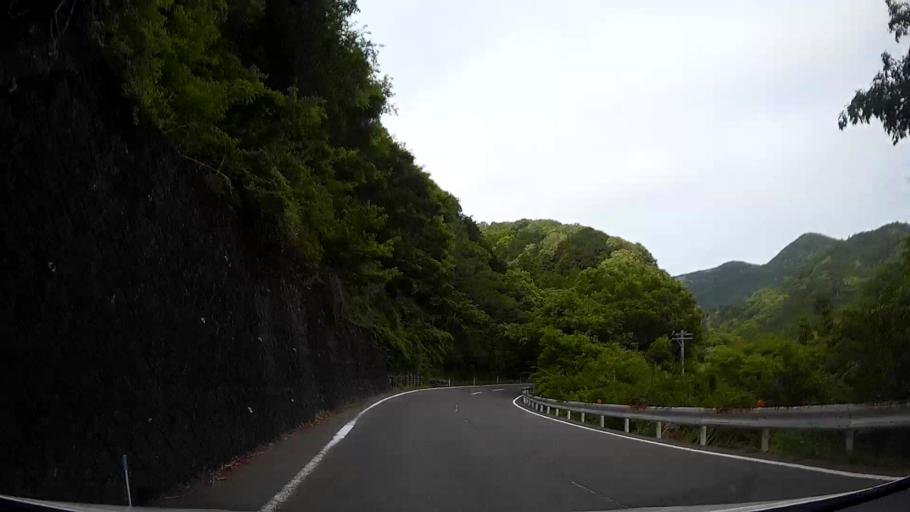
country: JP
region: Shizuoka
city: Ito
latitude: 34.9671
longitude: 139.0399
